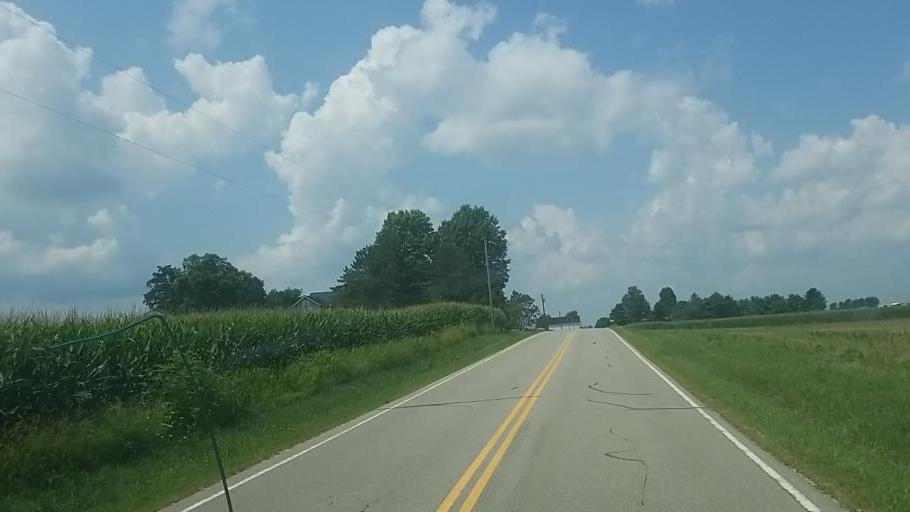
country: US
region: Ohio
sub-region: Crawford County
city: Bucyrus
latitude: 40.7986
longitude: -82.8739
